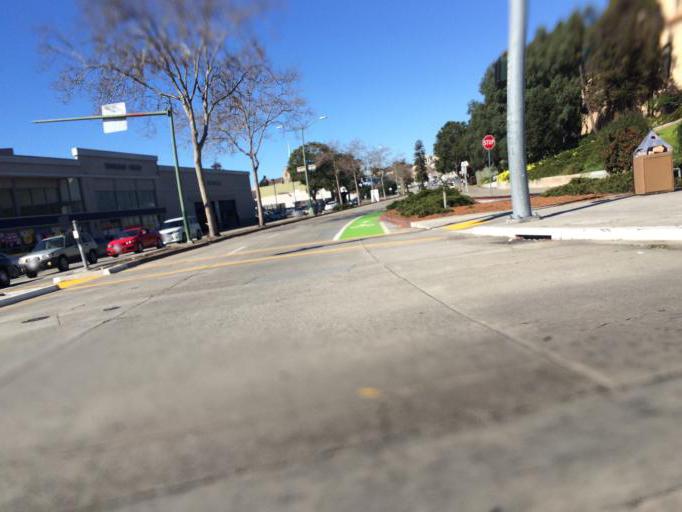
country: US
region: California
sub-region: Alameda County
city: Oakland
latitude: 37.8129
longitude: -122.2616
